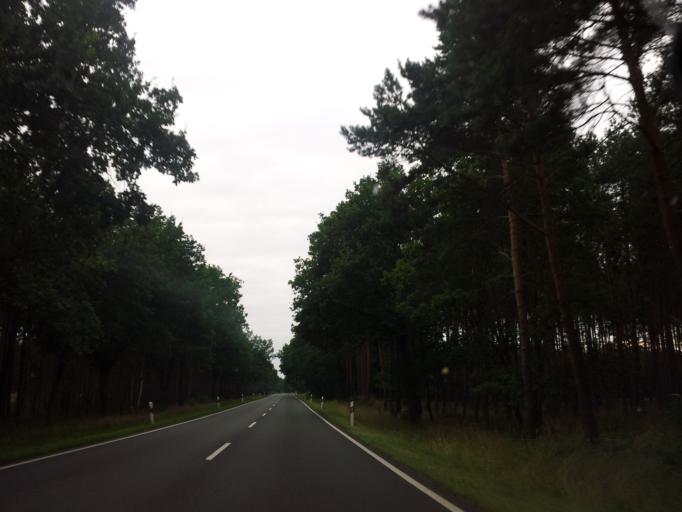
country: DE
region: Brandenburg
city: Niedergorsdorf
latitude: 52.0386
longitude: 12.9332
